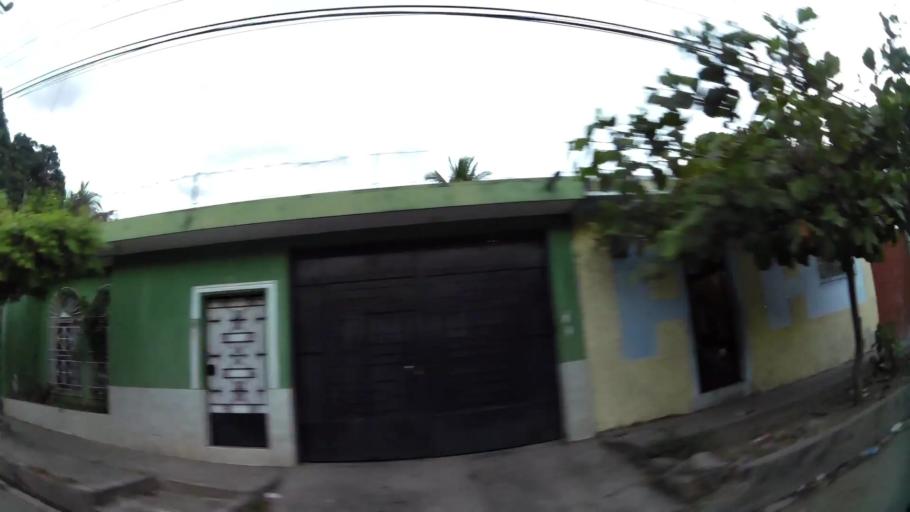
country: SV
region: San Vicente
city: San Vicente
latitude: 13.6427
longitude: -88.7919
